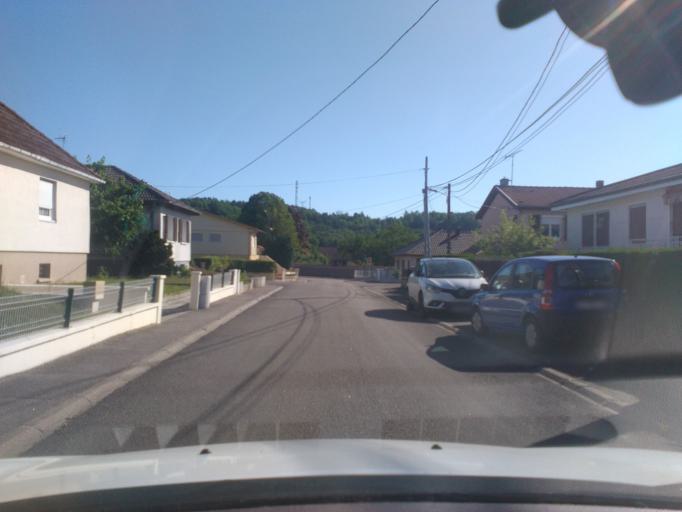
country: FR
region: Lorraine
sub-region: Departement des Vosges
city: Mirecourt
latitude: 48.2819
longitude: 6.1322
